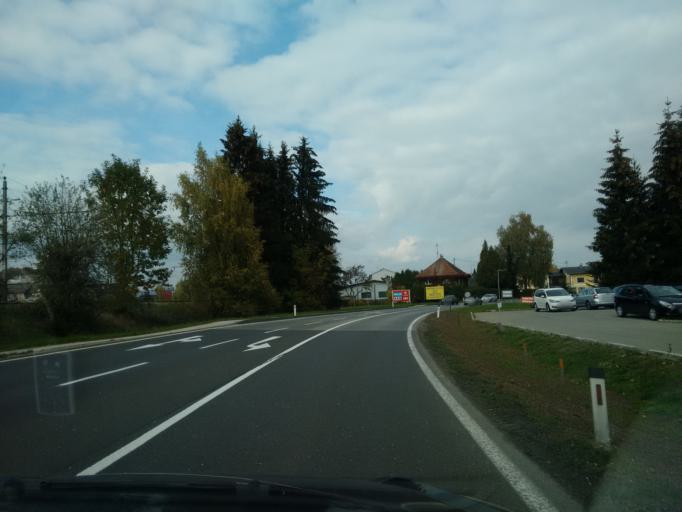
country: AT
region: Upper Austria
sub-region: Politischer Bezirk Vocklabruck
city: Lenzing
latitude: 47.9837
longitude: 13.6139
